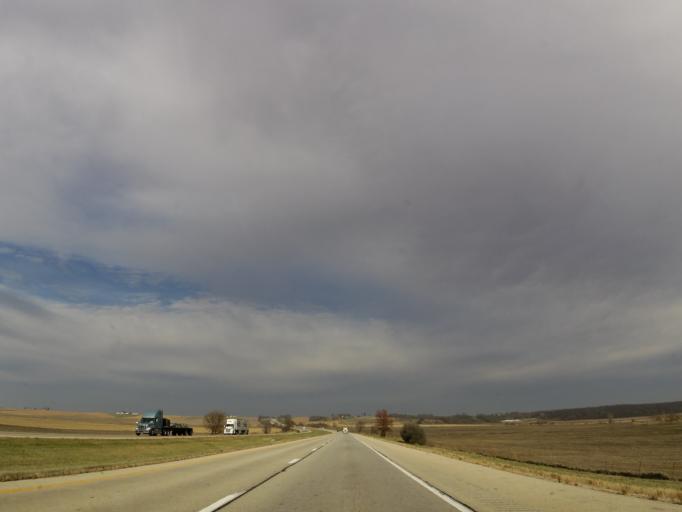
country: US
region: Illinois
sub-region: Henry County
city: Orion
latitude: 41.2561
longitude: -90.3296
